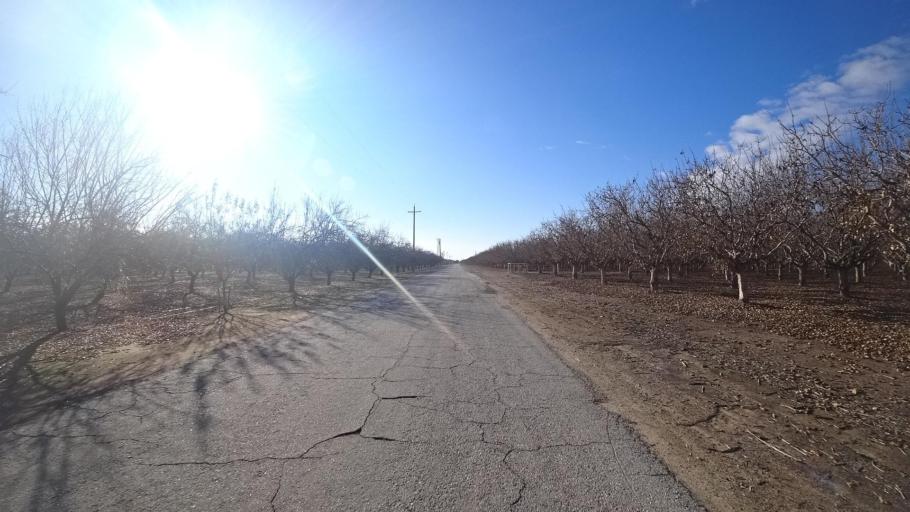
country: US
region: California
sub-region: Kern County
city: McFarland
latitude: 35.6939
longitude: -119.2942
